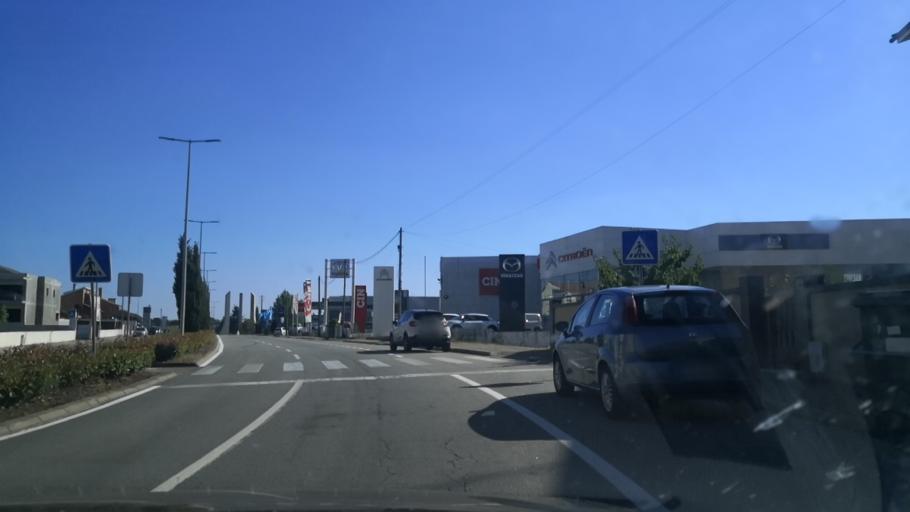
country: PT
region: Braganca
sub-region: Braganca Municipality
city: Braganca
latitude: 41.7825
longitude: -6.7782
